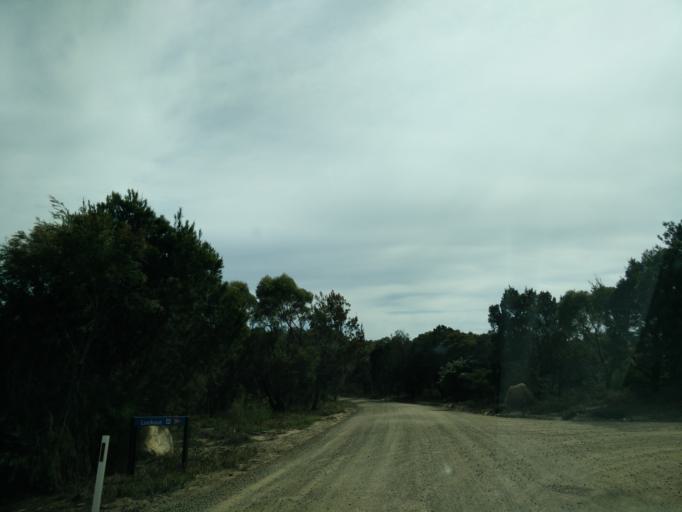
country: AU
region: Tasmania
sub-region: Break O'Day
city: St Helens
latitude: -41.9946
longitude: 148.2793
